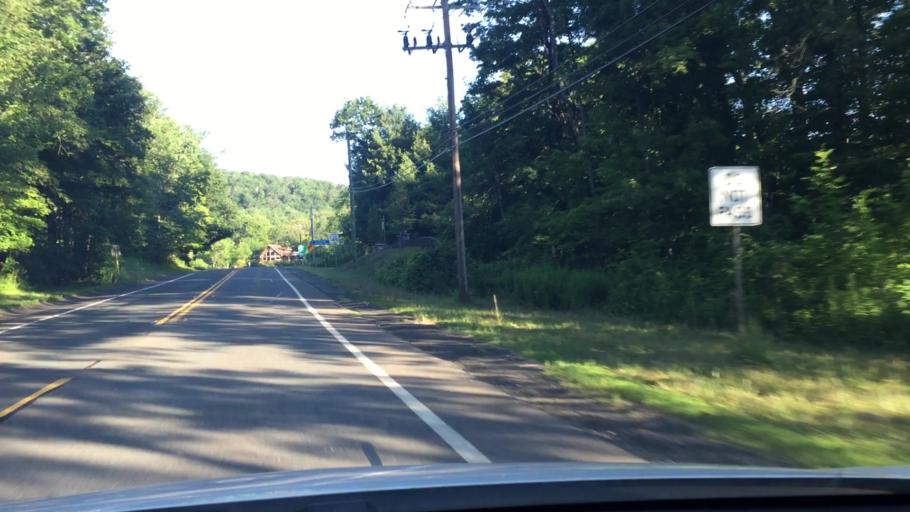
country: US
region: Massachusetts
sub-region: Berkshire County
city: Otis
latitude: 42.2632
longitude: -73.1317
